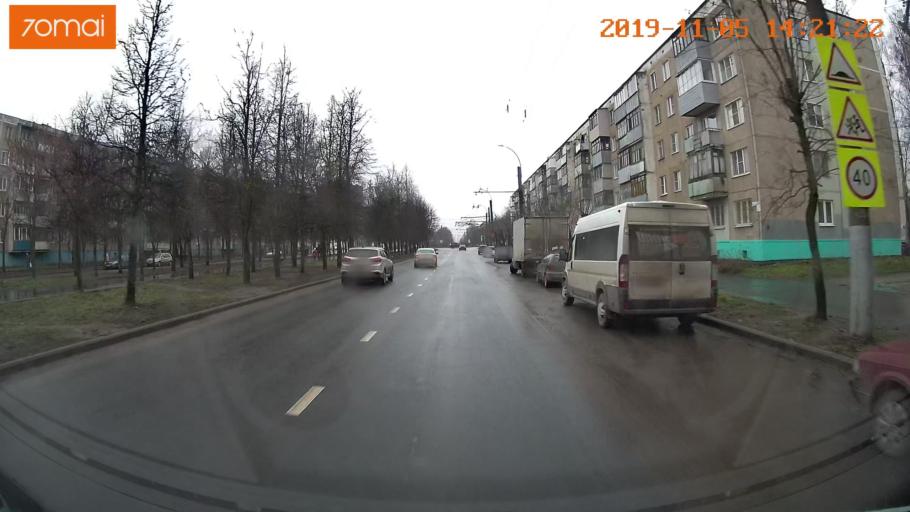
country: RU
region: Ivanovo
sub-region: Gorod Ivanovo
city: Ivanovo
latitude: 56.9590
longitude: 41.0113
